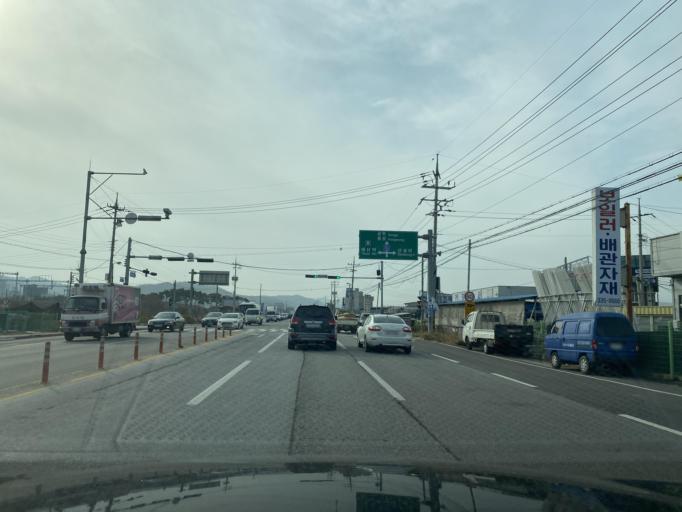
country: KR
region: Chungcheongnam-do
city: Yesan
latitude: 36.6915
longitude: 126.8278
